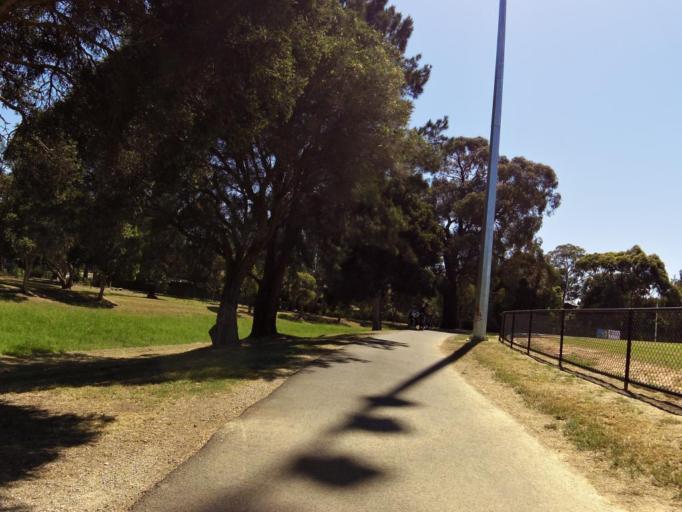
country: AU
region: Victoria
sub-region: Knox
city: Bayswater
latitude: -37.8684
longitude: 145.2625
